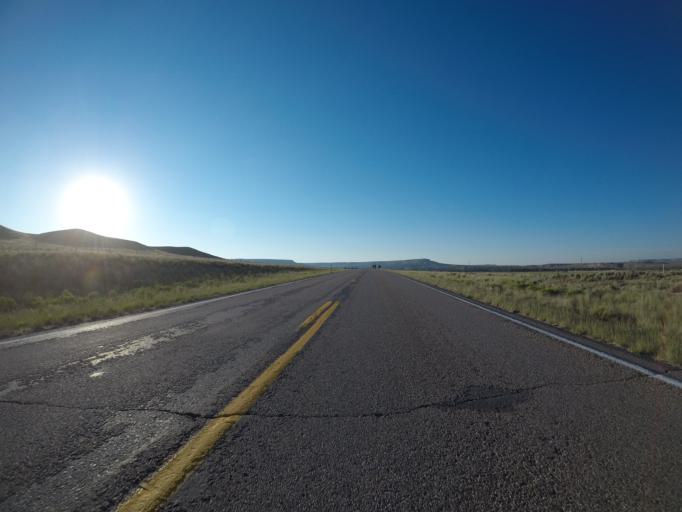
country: US
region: Wyoming
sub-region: Sublette County
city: Marbleton
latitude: 42.5744
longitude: -109.9796
